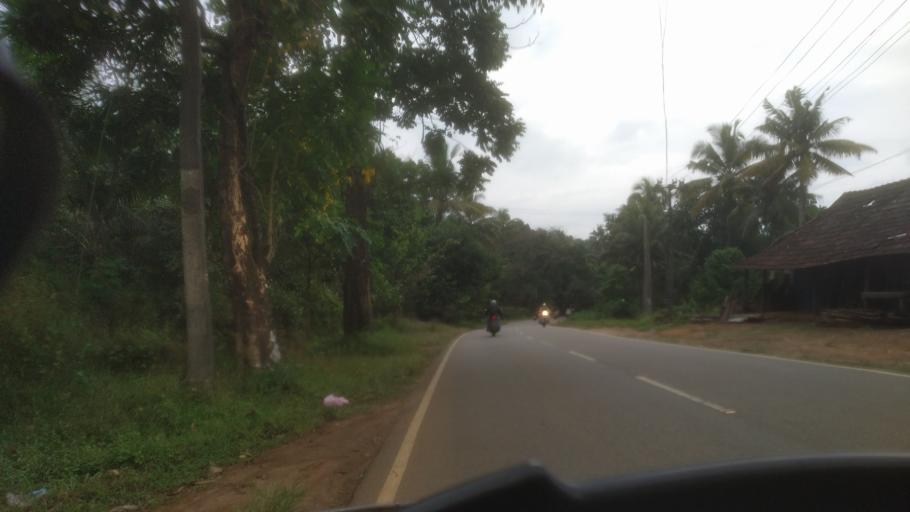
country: IN
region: Kerala
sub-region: Idukki
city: Munnar
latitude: 9.9989
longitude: 76.9705
